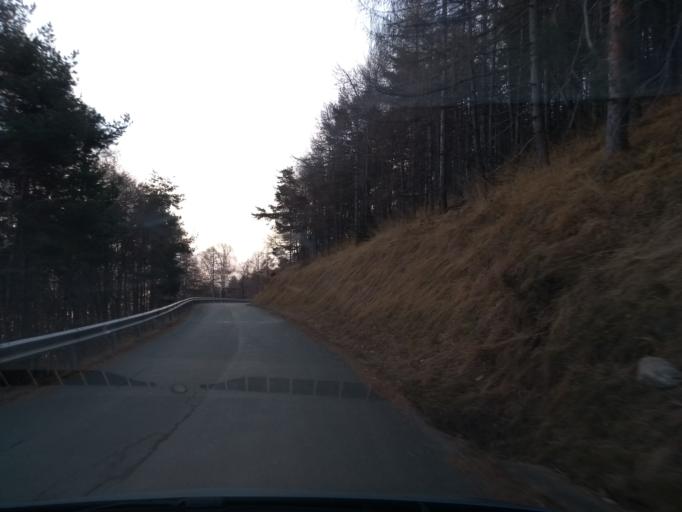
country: IT
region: Piedmont
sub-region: Provincia di Torino
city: Coassolo Torinese
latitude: 45.2811
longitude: 7.4514
